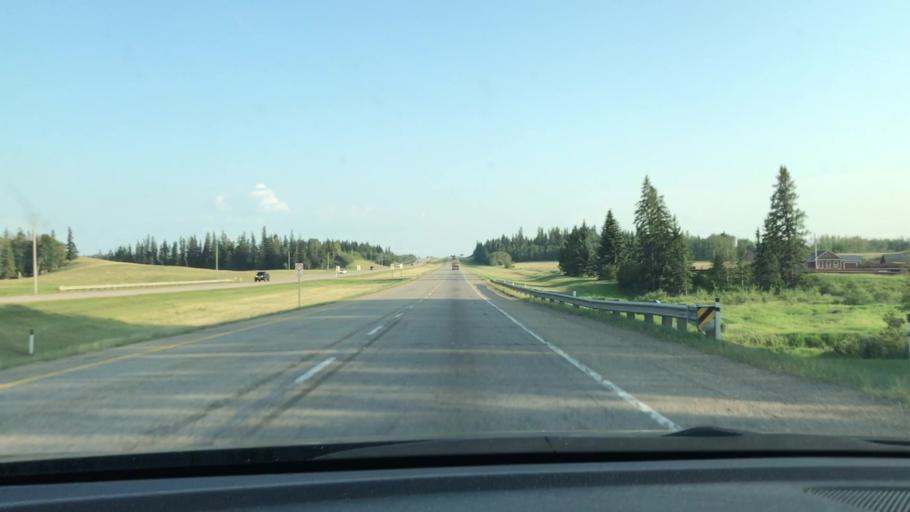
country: CA
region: Alberta
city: Ponoka
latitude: 52.6016
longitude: -113.6635
